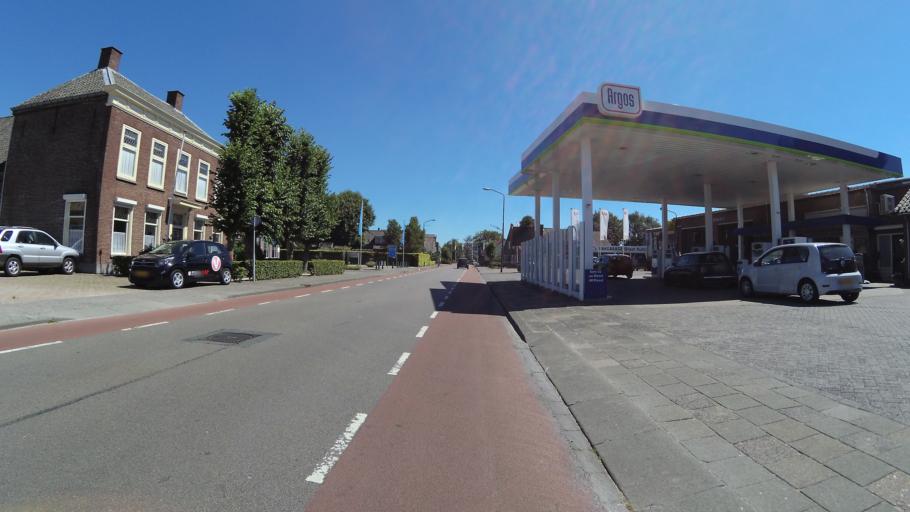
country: NL
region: North Brabant
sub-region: Gemeente Waalwijk
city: Waalwijk
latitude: 51.6701
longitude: 5.0283
